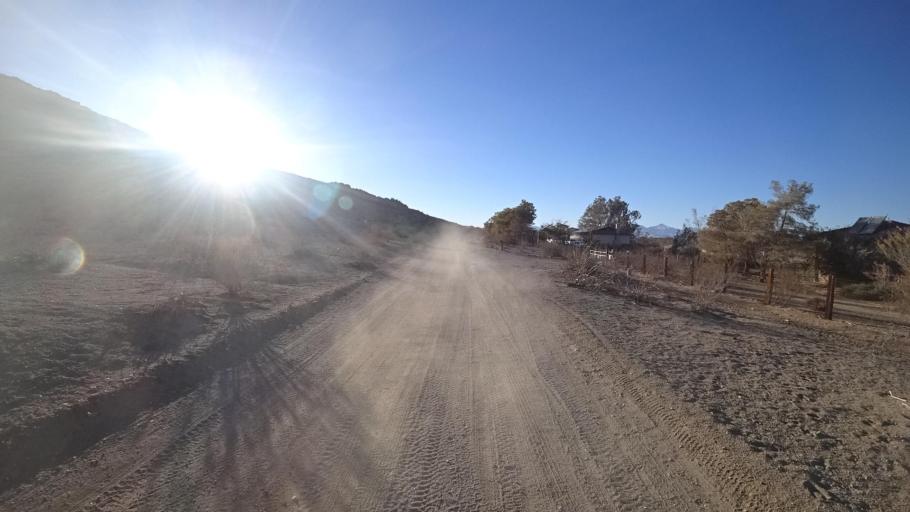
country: US
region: California
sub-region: Kern County
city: Ridgecrest
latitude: 35.5788
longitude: -117.6573
